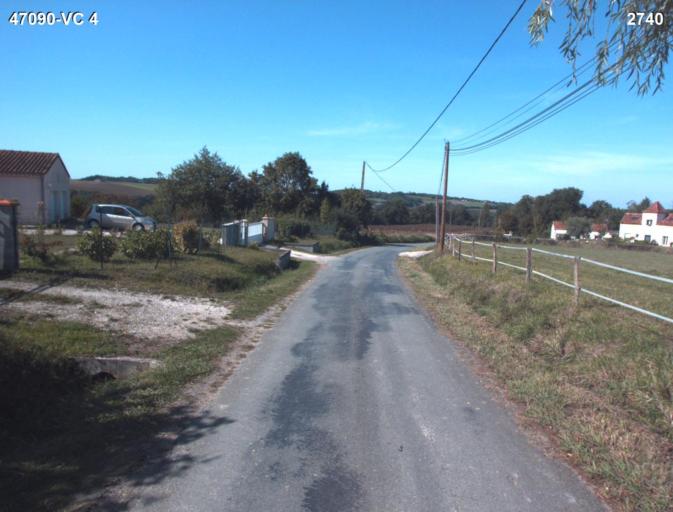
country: FR
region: Aquitaine
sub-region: Departement du Lot-et-Garonne
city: Nerac
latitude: 44.1718
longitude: 0.3709
